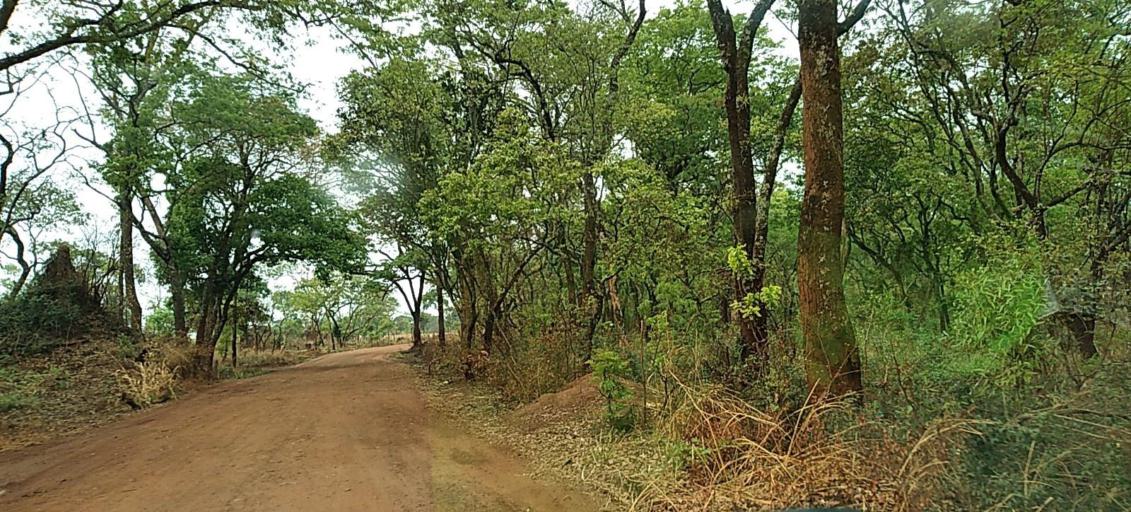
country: ZM
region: North-Western
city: Solwezi
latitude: -12.3152
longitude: 26.5222
